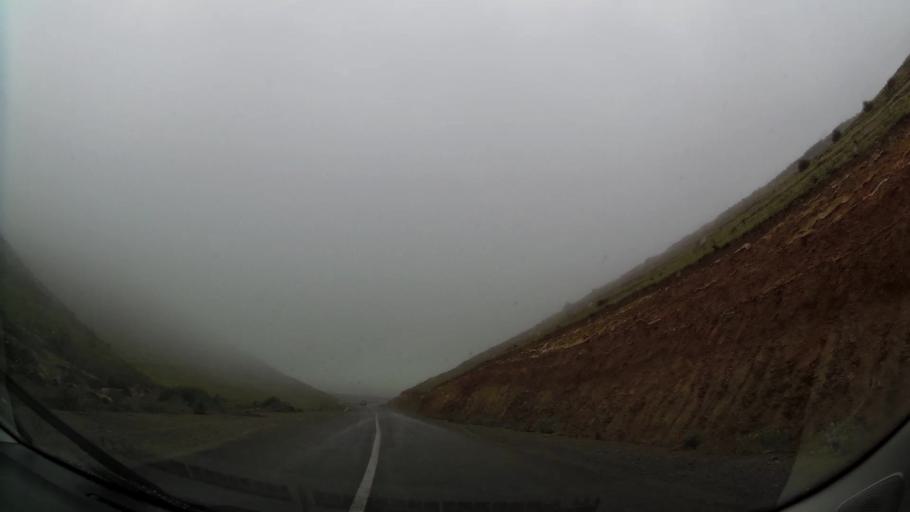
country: MA
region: Oriental
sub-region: Nador
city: Boudinar
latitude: 35.1077
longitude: -3.5670
